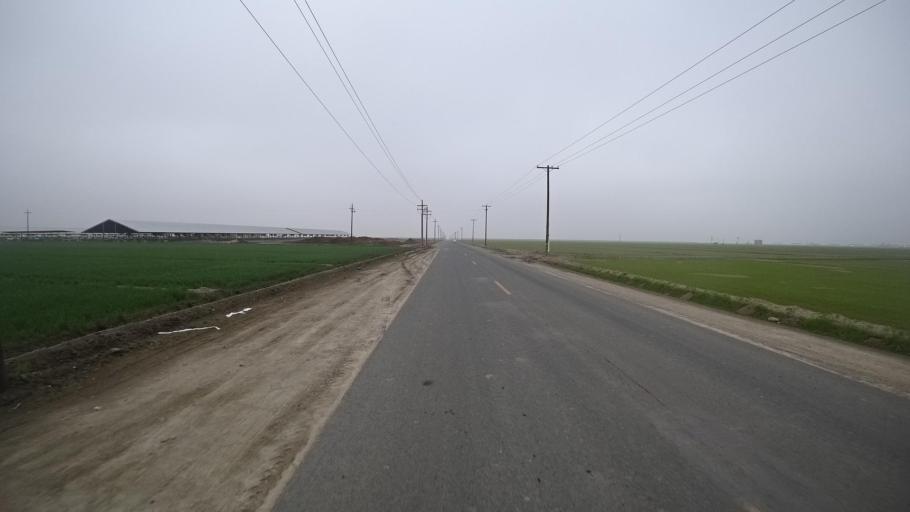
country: US
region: California
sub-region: Kern County
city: Wasco
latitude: 35.7175
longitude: -119.4235
